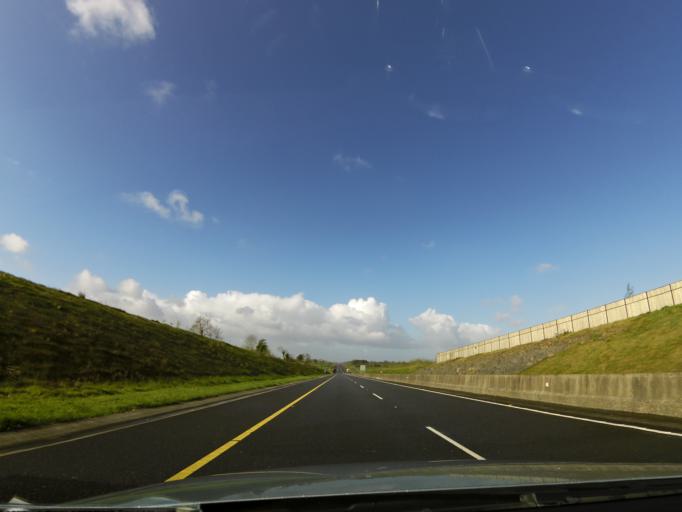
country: IE
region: Munster
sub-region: North Tipperary
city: Newport
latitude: 52.7447
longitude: -8.4357
